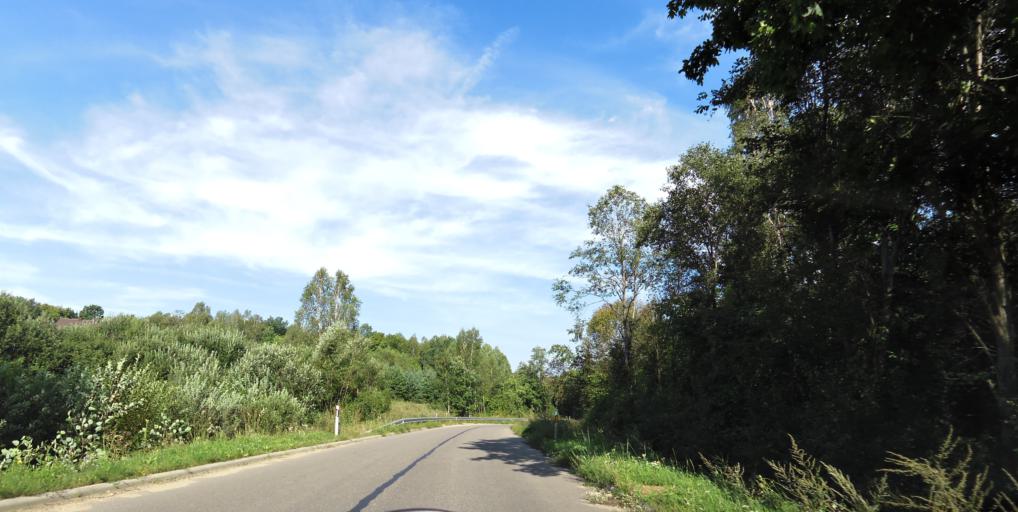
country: LT
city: Grigiskes
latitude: 54.7266
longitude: 25.0711
